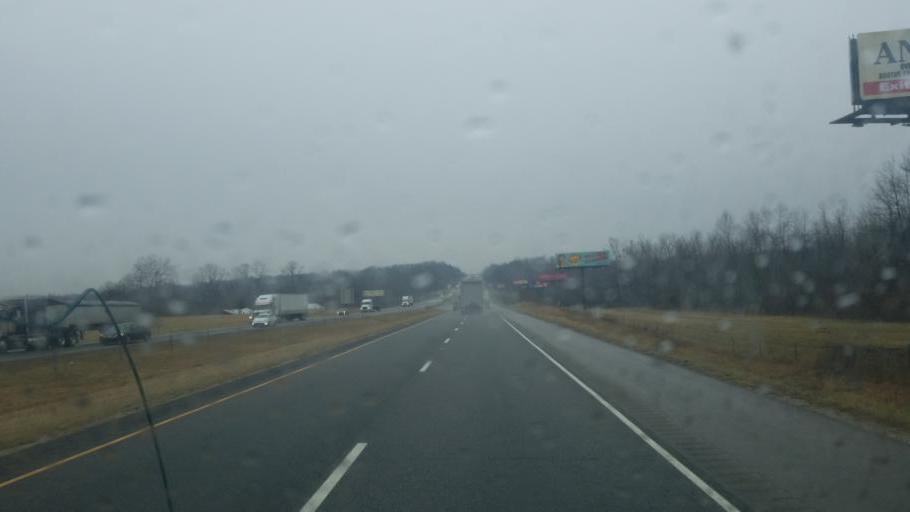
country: US
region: Ohio
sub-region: Preble County
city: New Paris
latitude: 39.8435
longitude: -84.8276
